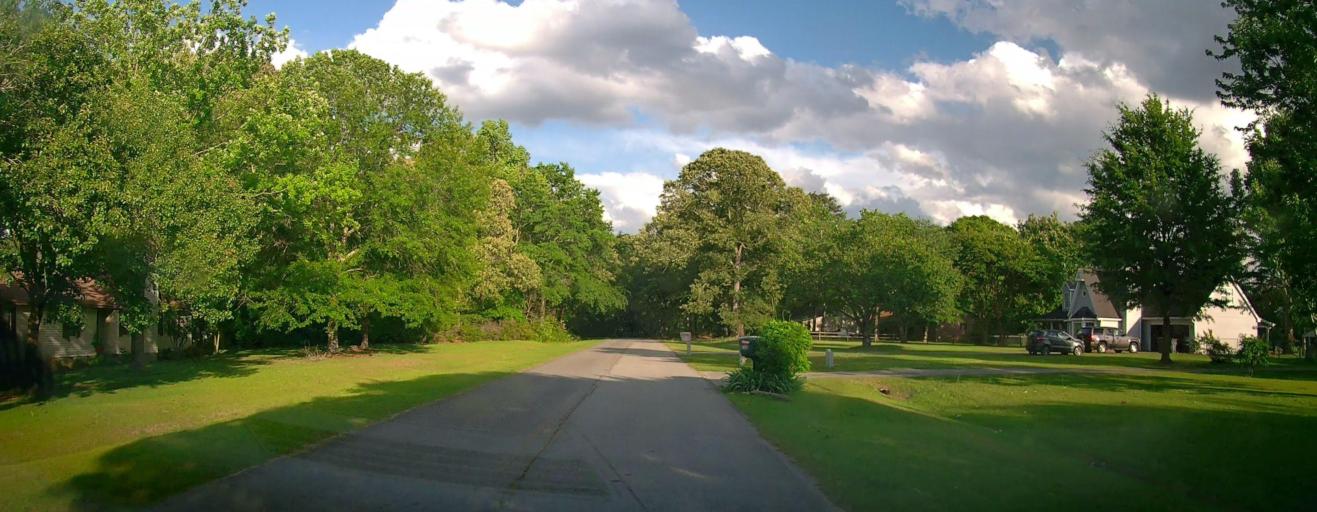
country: US
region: Georgia
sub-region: Peach County
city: Byron
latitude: 32.6353
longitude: -83.7535
